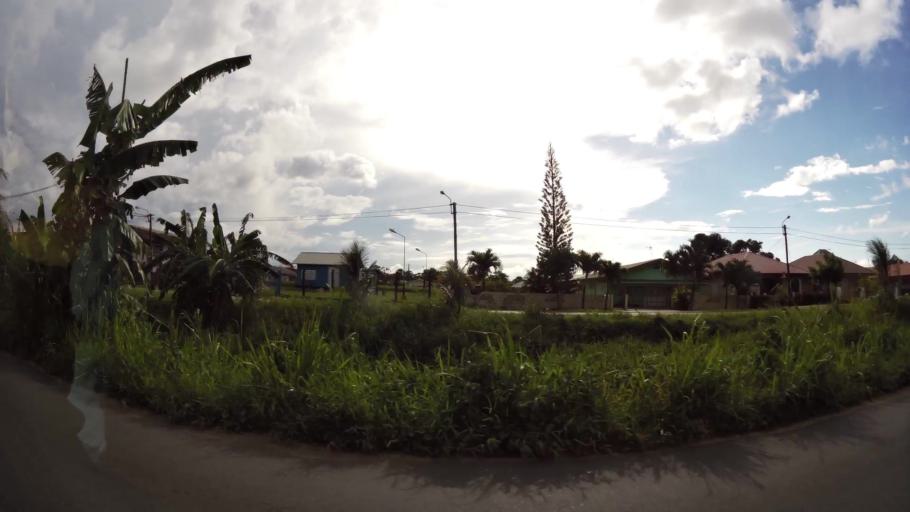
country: SR
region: Paramaribo
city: Paramaribo
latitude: 5.8576
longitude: -55.1833
